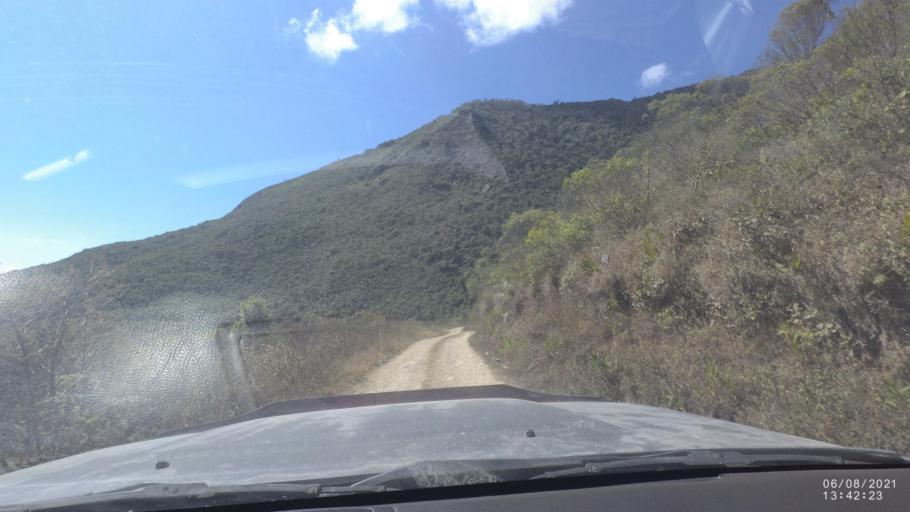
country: BO
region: La Paz
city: Quime
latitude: -16.6802
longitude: -66.7300
